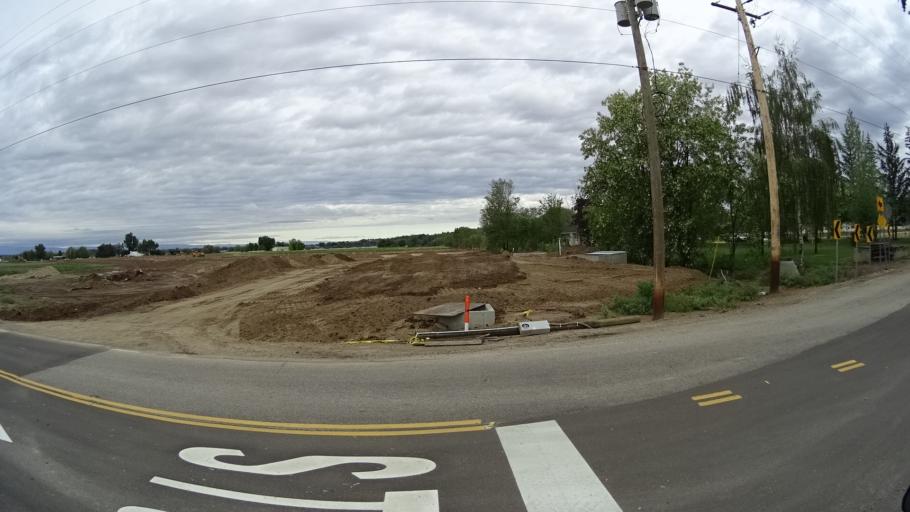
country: US
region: Idaho
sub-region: Ada County
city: Star
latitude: 43.7211
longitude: -116.4831
